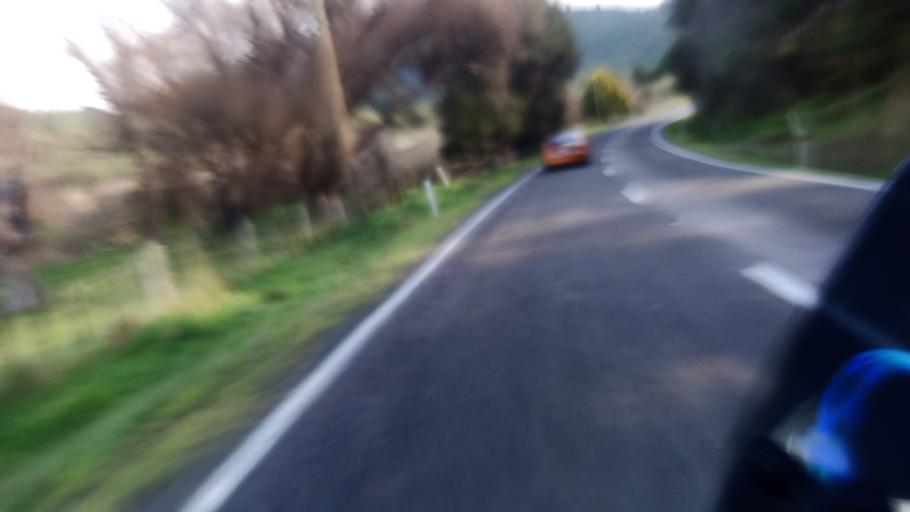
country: NZ
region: Gisborne
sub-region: Gisborne District
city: Gisborne
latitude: -38.1160
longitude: 178.2975
